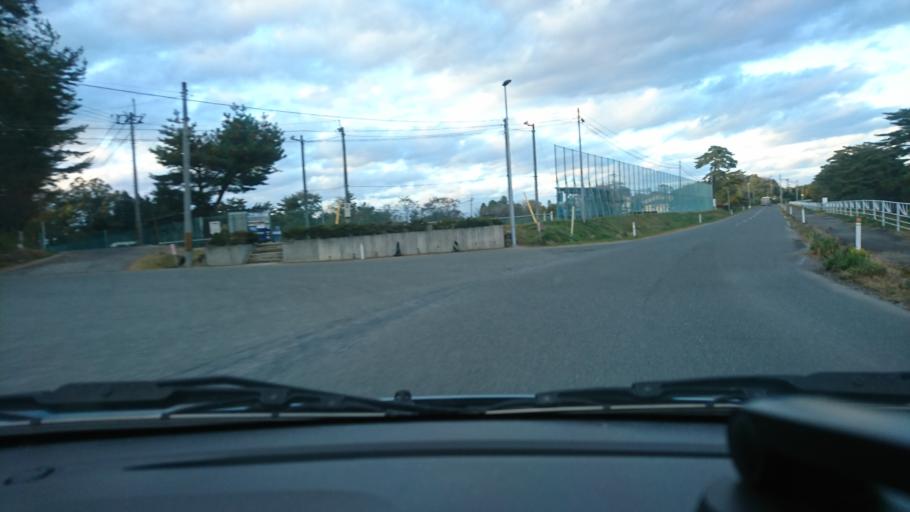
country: JP
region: Iwate
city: Ichinoseki
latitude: 38.8045
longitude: 141.1918
